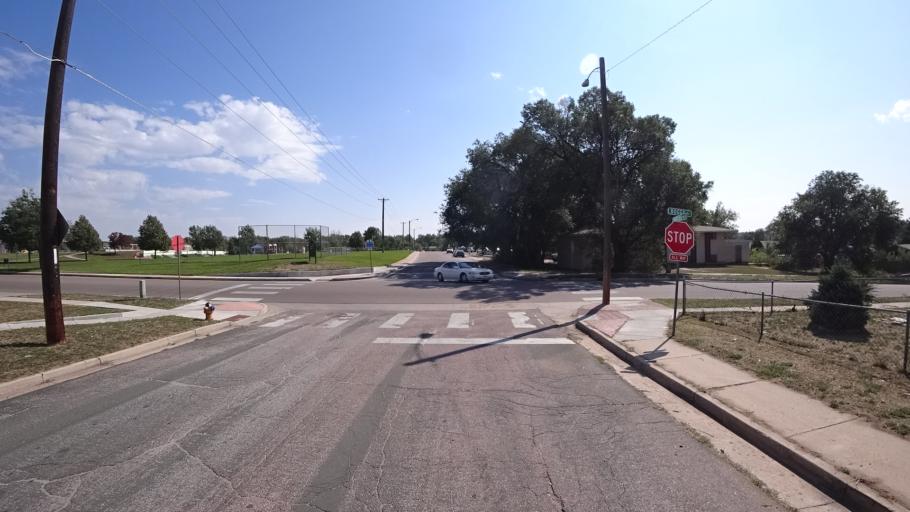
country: US
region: Colorado
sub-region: El Paso County
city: Colorado Springs
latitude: 38.8198
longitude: -104.7900
